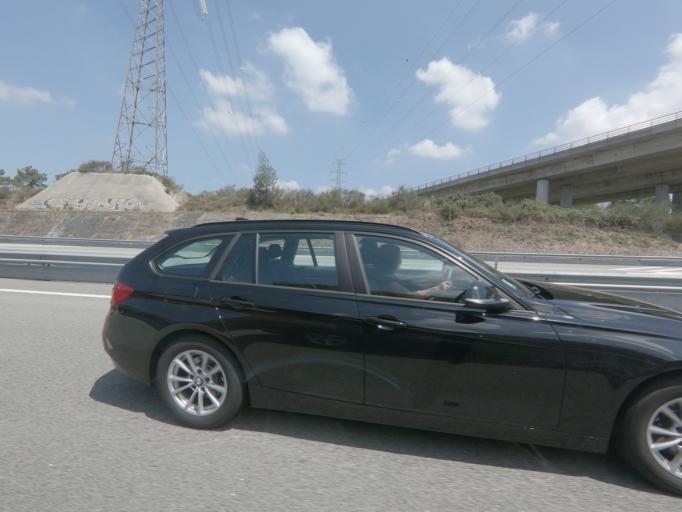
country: PT
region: Porto
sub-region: Valongo
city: Campo
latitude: 41.1860
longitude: -8.4554
